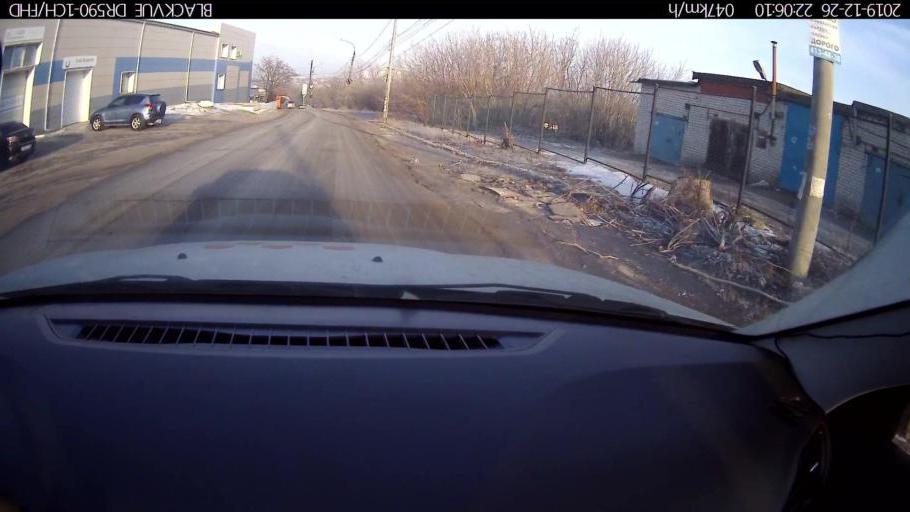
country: RU
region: Nizjnij Novgorod
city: Nizhniy Novgorod
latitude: 56.2377
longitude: 43.9947
